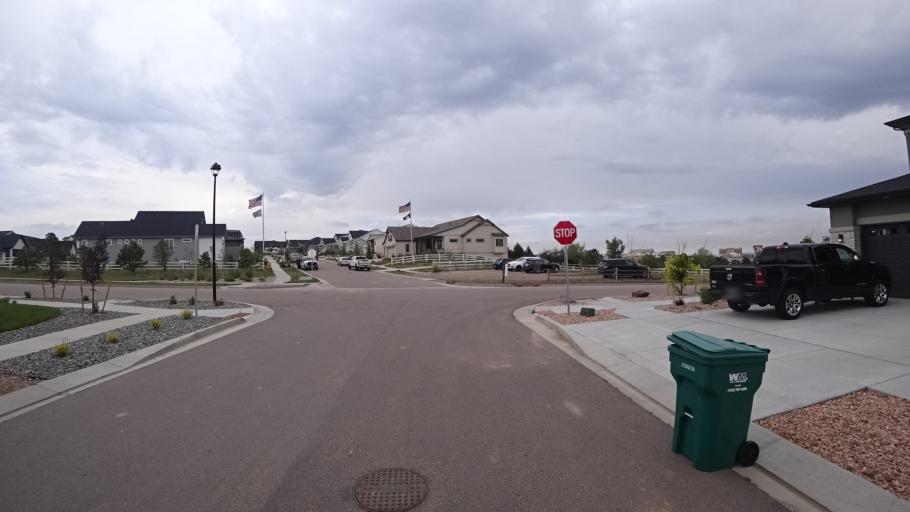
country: US
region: Colorado
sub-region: El Paso County
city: Gleneagle
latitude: 39.0037
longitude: -104.8101
